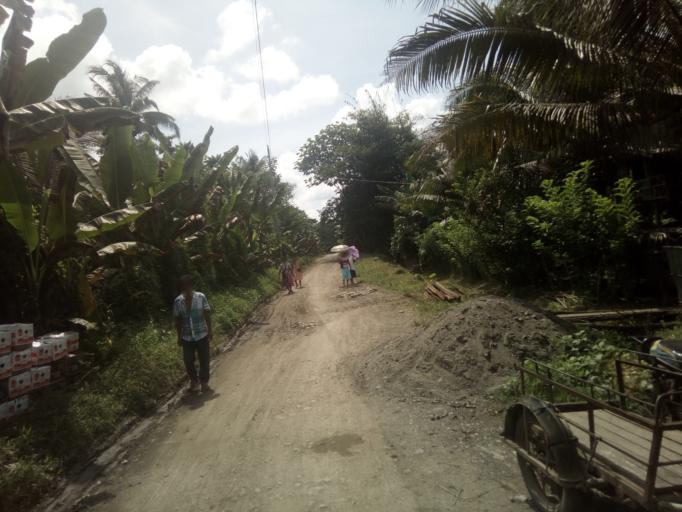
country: PH
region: Caraga
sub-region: Province of Agusan del Sur
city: Santa Josefa
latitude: 8.0364
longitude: 126.0120
